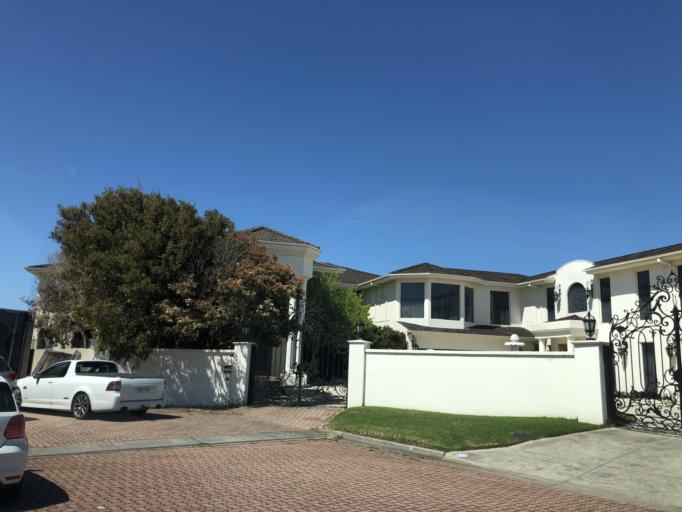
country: AU
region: Victoria
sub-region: Kingston
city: Carrum
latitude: -38.0805
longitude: 145.1412
